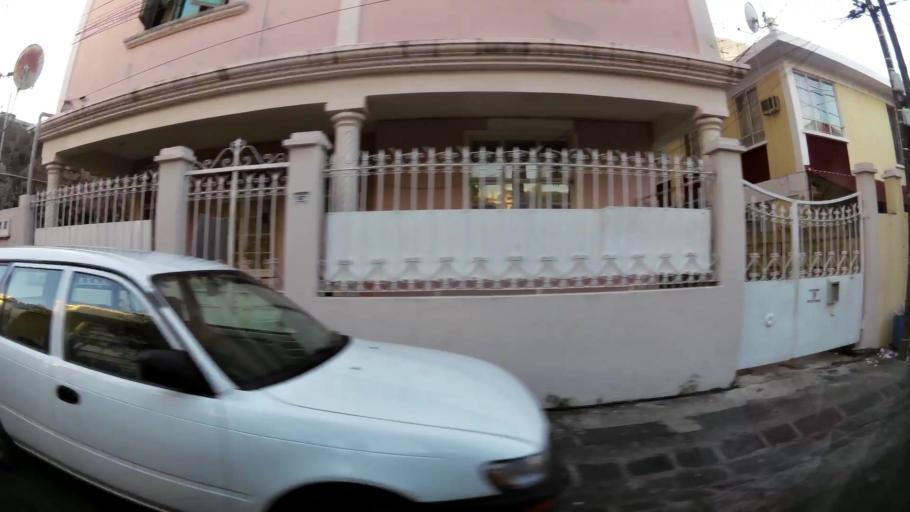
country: MU
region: Port Louis
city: Port Louis
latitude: -20.1703
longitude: 57.5019
